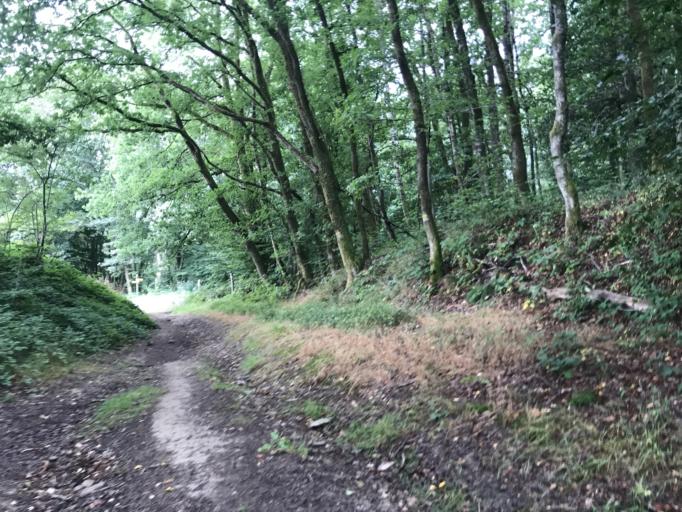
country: FR
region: Champagne-Ardenne
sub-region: Departement des Ardennes
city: Thilay
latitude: 49.8772
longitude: 4.7913
